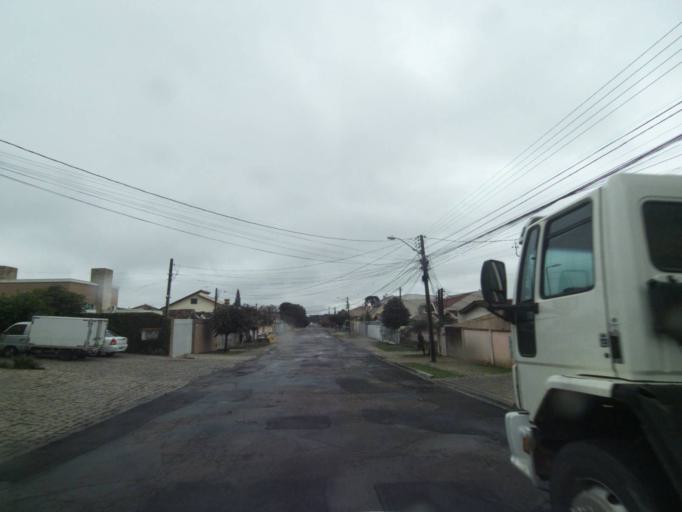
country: BR
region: Parana
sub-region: Curitiba
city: Curitiba
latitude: -25.5103
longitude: -49.2994
